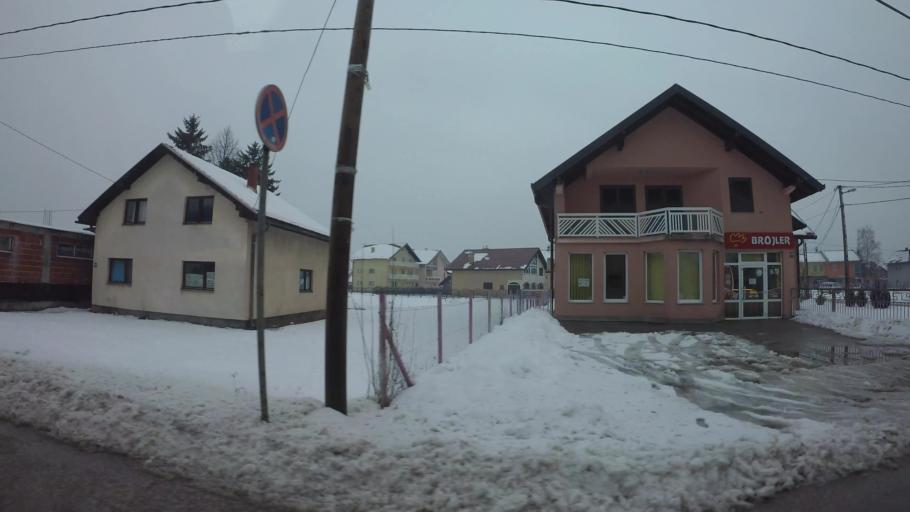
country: BA
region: Federation of Bosnia and Herzegovina
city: Hadzici
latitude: 43.8443
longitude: 18.2774
